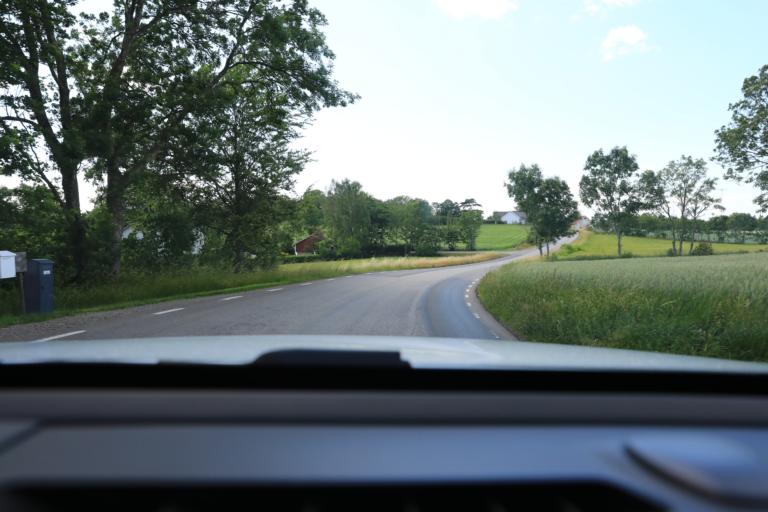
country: SE
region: Halland
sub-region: Varbergs Kommun
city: Tvaaker
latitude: 57.1099
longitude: 12.4223
